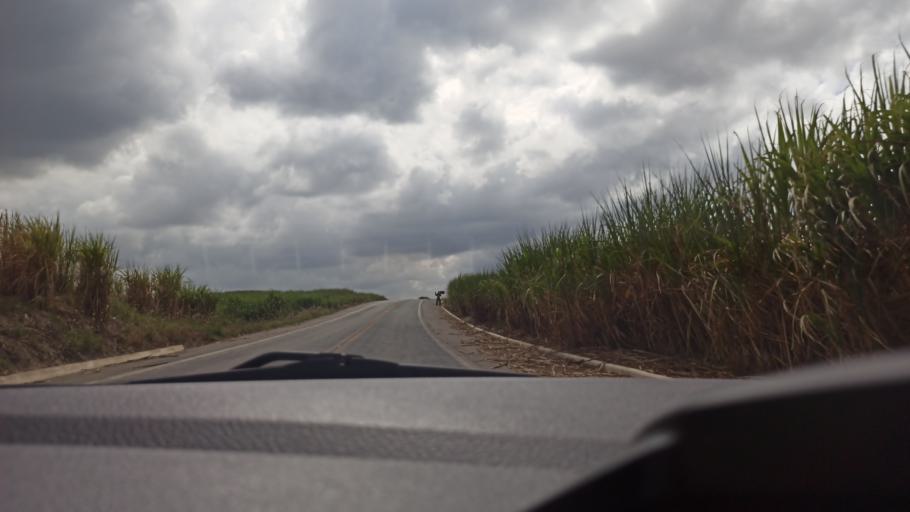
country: BR
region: Pernambuco
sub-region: Timbauba
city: Timbauba
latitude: -7.5449
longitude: -35.2699
